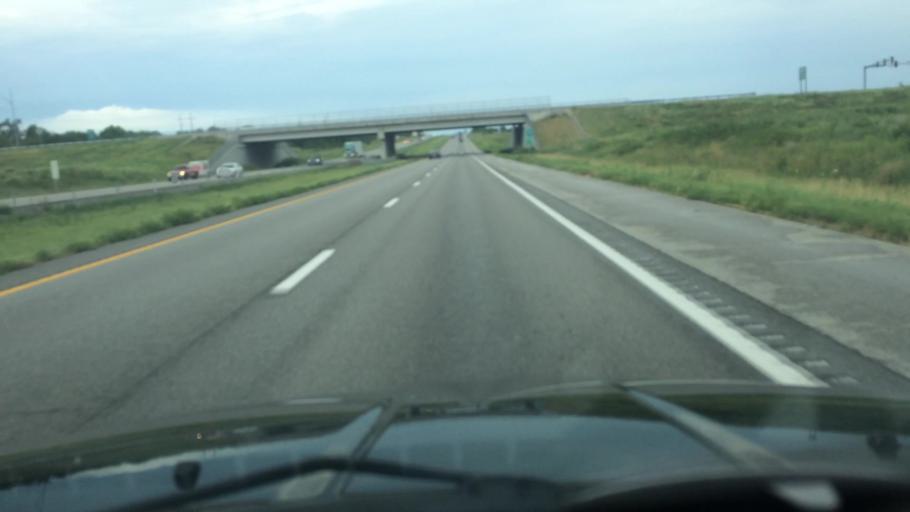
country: US
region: Missouri
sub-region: Cass County
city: Belton
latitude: 38.7845
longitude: -94.4969
